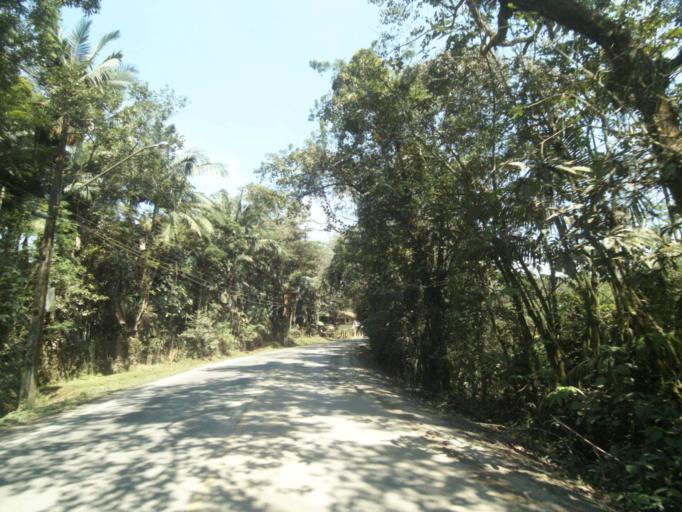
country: BR
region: Parana
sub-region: Paranagua
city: Paranagua
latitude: -25.5609
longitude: -48.6256
